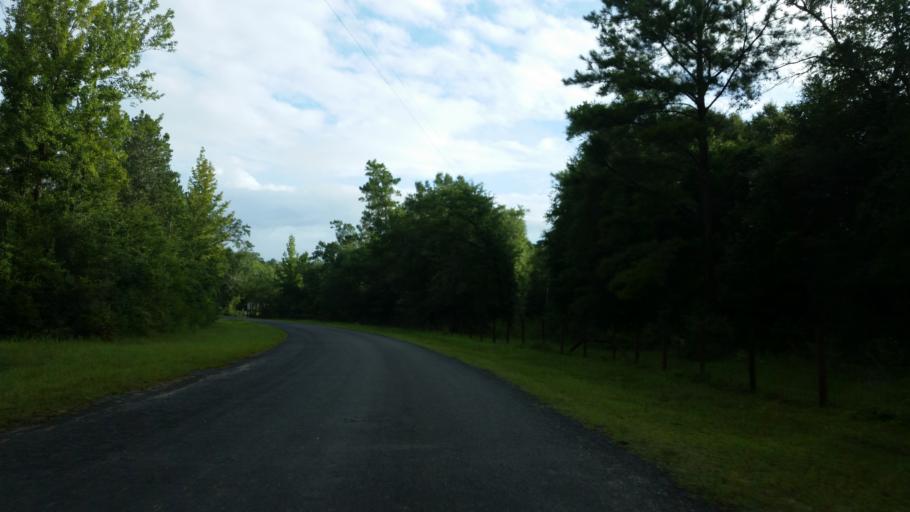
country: US
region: Florida
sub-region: Okaloosa County
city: Crestview
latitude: 30.6786
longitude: -86.7486
